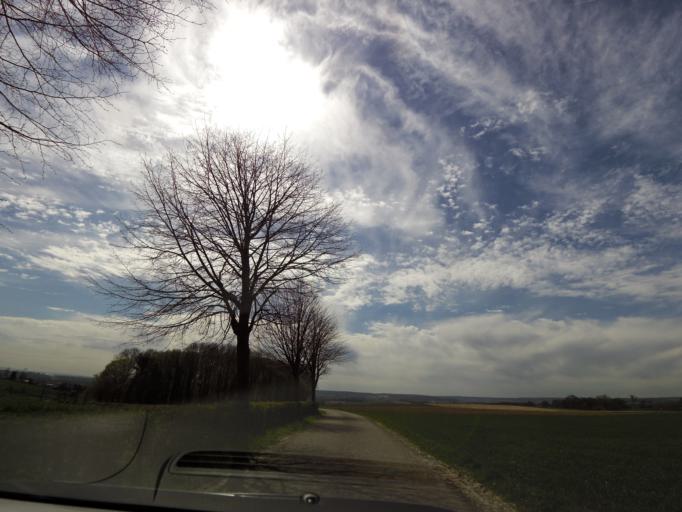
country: NL
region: Limburg
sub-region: Gemeente Voerendaal
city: Ubachsberg
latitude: 50.8442
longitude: 5.9648
